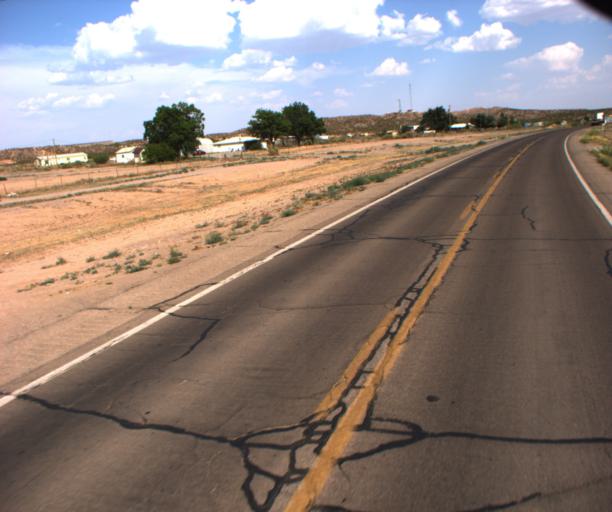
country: US
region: Arizona
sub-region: Greenlee County
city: Clifton
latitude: 32.7400
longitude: -109.0954
